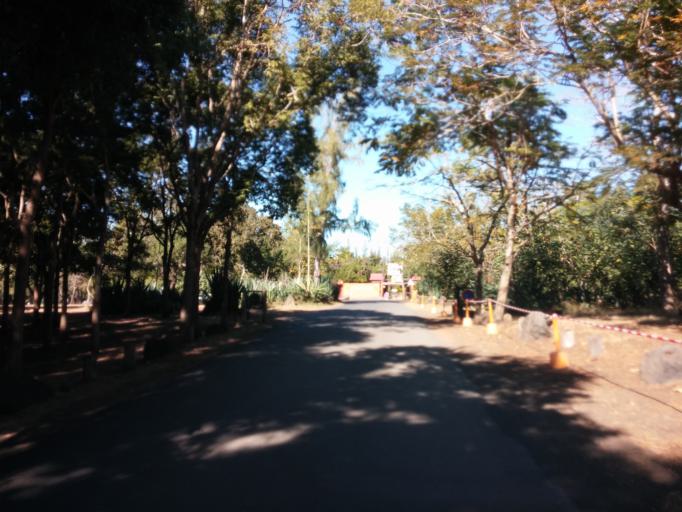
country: RE
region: Reunion
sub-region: Reunion
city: Les Avirons
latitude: -21.2662
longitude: 55.3532
